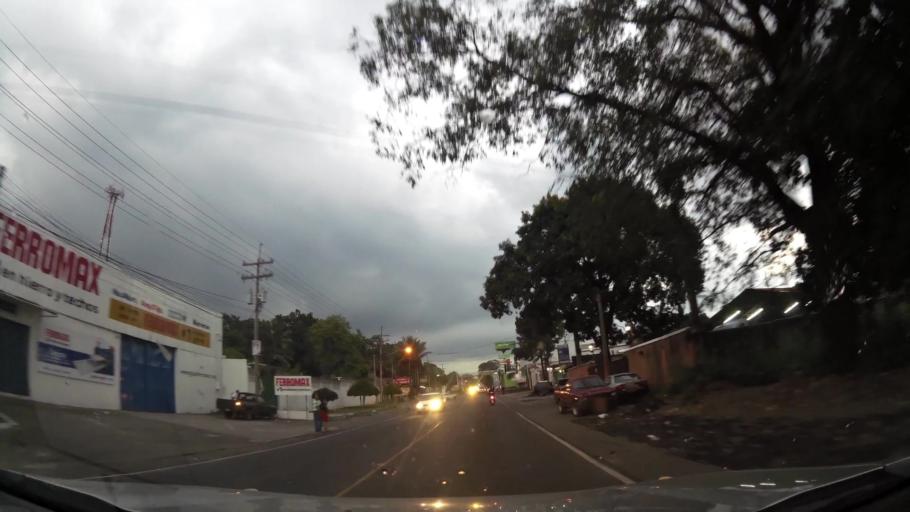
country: GT
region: Escuintla
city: Santa Lucia Cotzumalguapa
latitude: 14.3292
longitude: -91.0203
